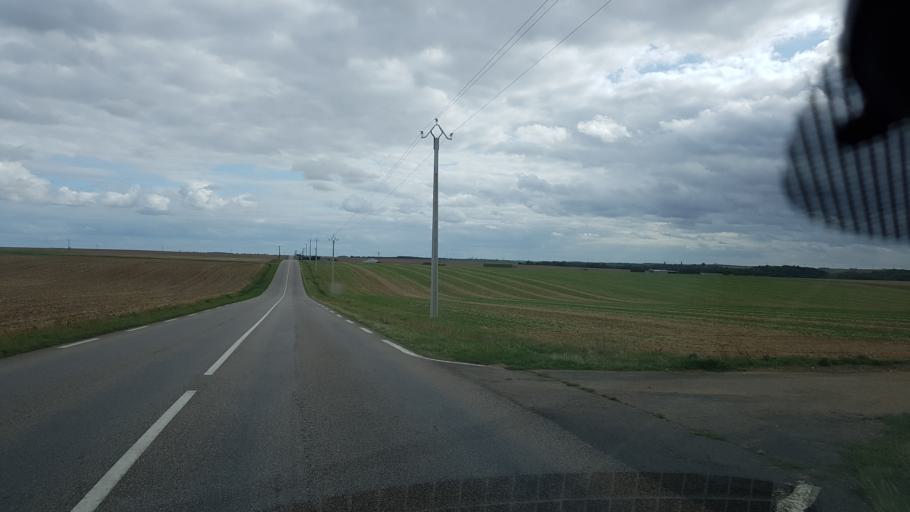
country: FR
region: Ile-de-France
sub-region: Departement de l'Essonne
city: Saclas
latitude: 48.3561
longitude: 2.1687
